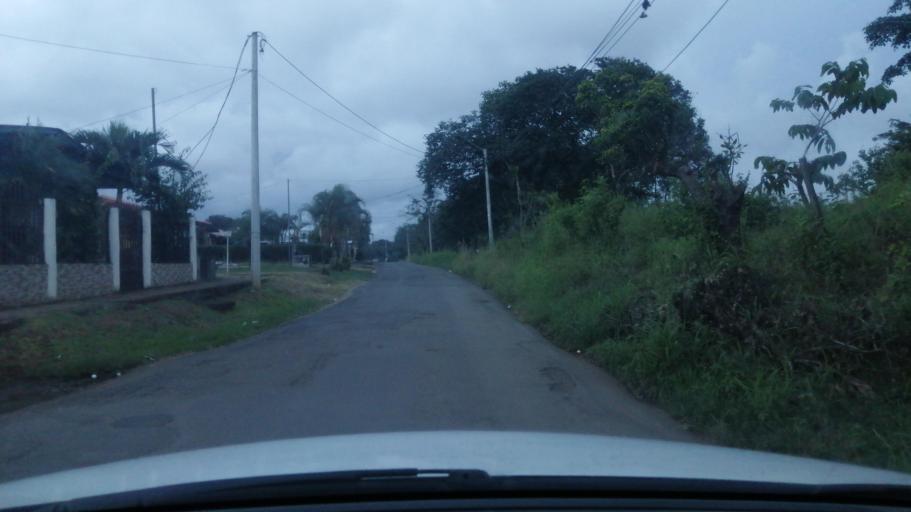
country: PA
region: Chiriqui
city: David
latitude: 8.4006
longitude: -82.4425
